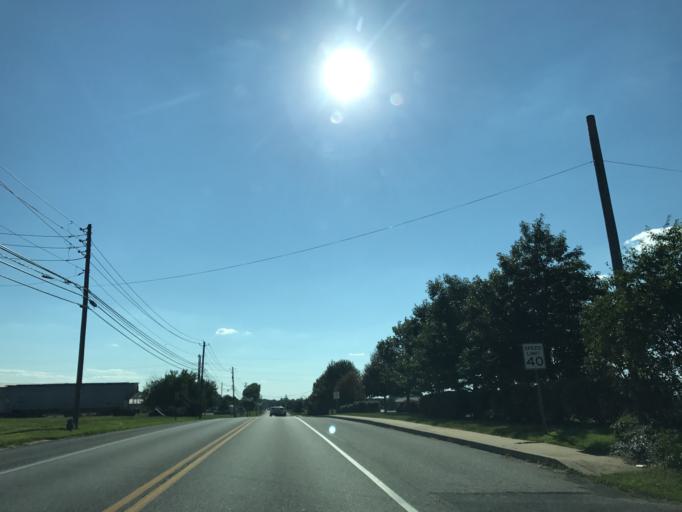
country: US
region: Pennsylvania
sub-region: Lancaster County
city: Mount Joy
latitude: 40.1106
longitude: -76.4698
